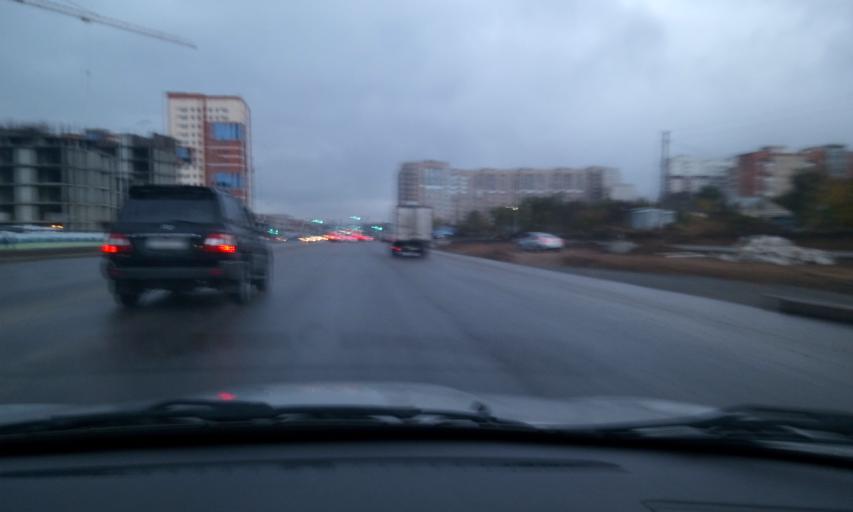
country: KZ
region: Astana Qalasy
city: Astana
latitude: 51.1272
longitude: 71.4987
